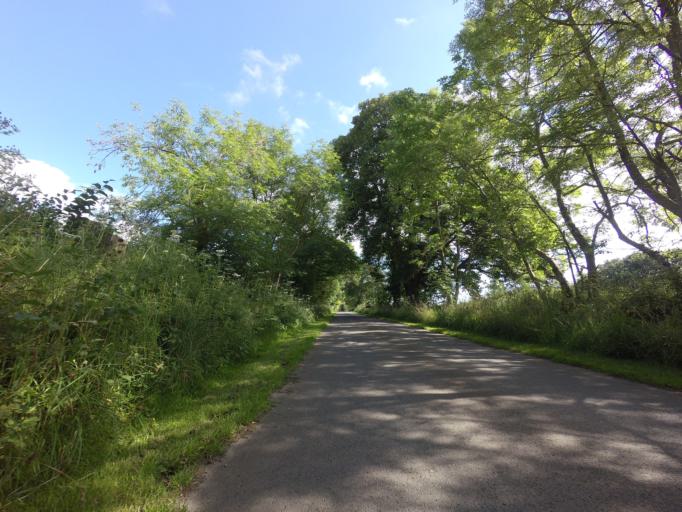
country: GB
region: Scotland
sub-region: Aberdeenshire
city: Turriff
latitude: 57.5918
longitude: -2.5066
